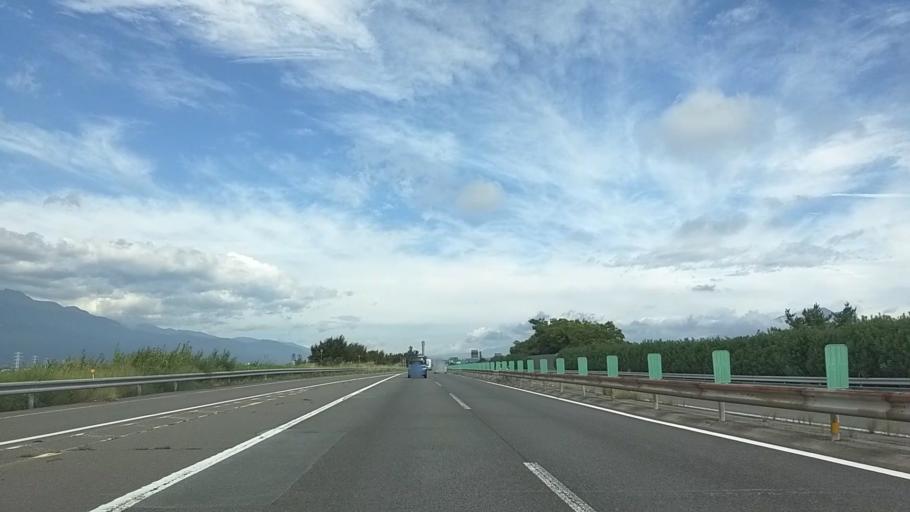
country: JP
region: Yamanashi
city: Kofu-shi
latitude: 35.6301
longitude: 138.5430
